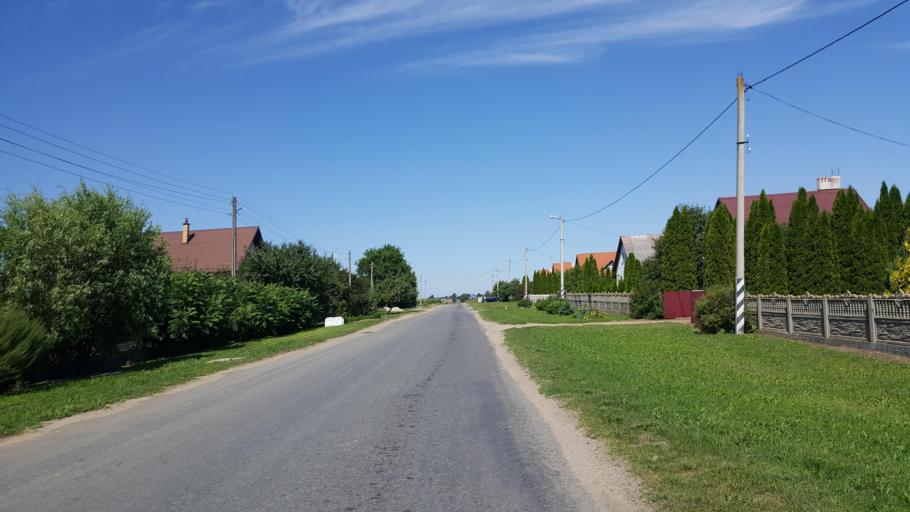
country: BY
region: Brest
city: Charnawchytsy
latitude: 52.2272
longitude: 23.7340
